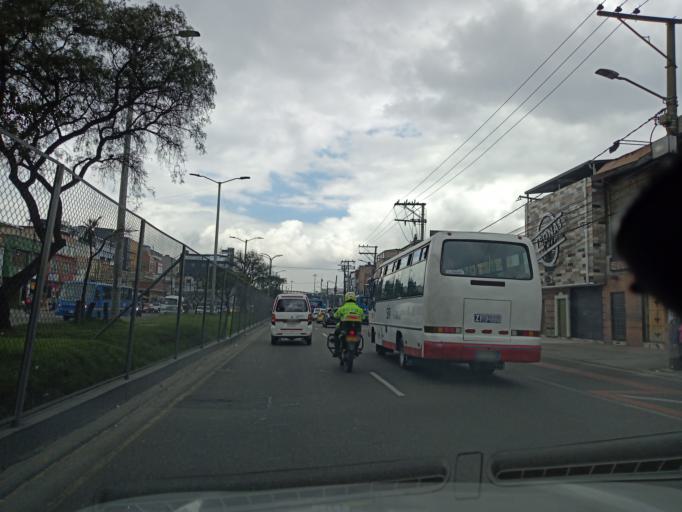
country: CO
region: Bogota D.C.
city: Bogota
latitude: 4.6152
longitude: -74.1363
